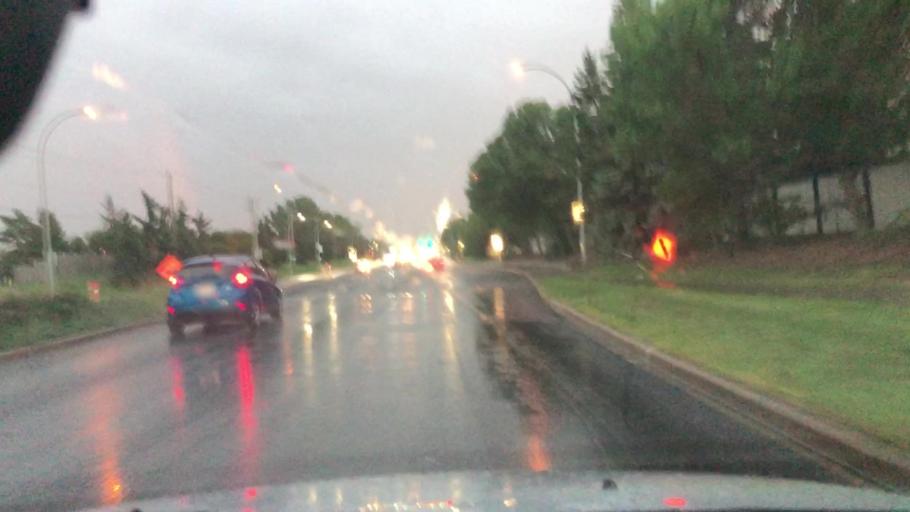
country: CA
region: Alberta
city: St. Albert
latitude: 53.6213
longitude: -113.5412
